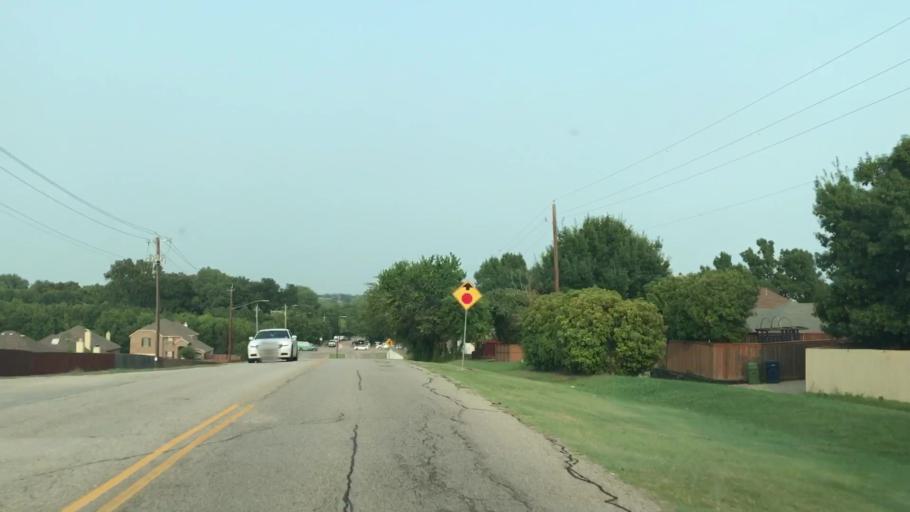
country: US
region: Texas
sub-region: Dallas County
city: Rowlett
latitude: 32.9196
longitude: -96.5995
